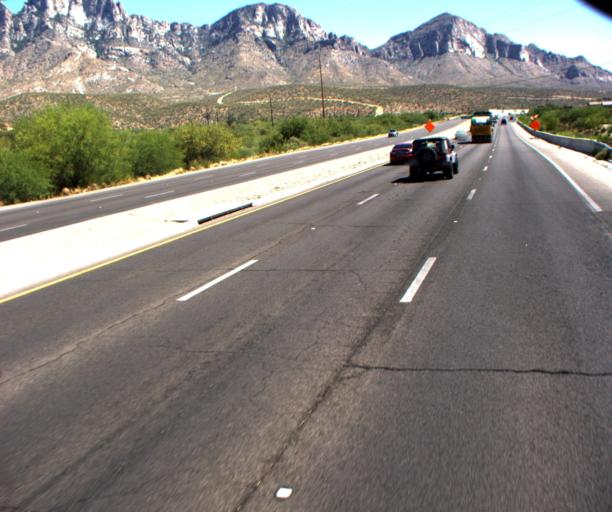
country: US
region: Arizona
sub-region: Pima County
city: Oro Valley
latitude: 32.4206
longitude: -110.9372
